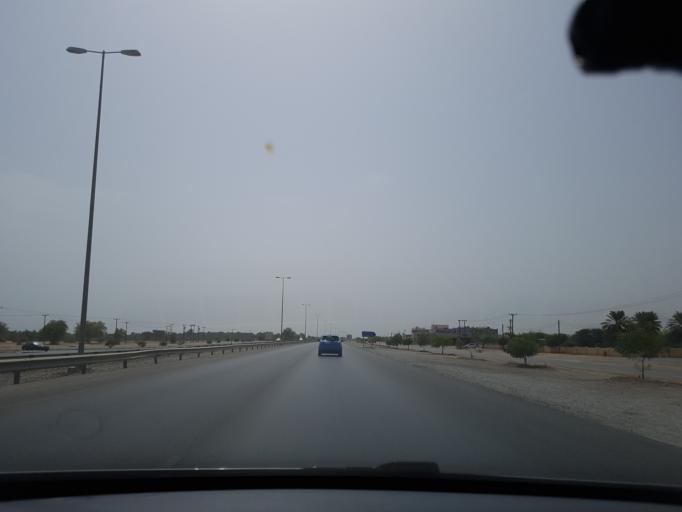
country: OM
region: Al Batinah
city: As Suwayq
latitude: 23.8163
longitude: 57.4499
